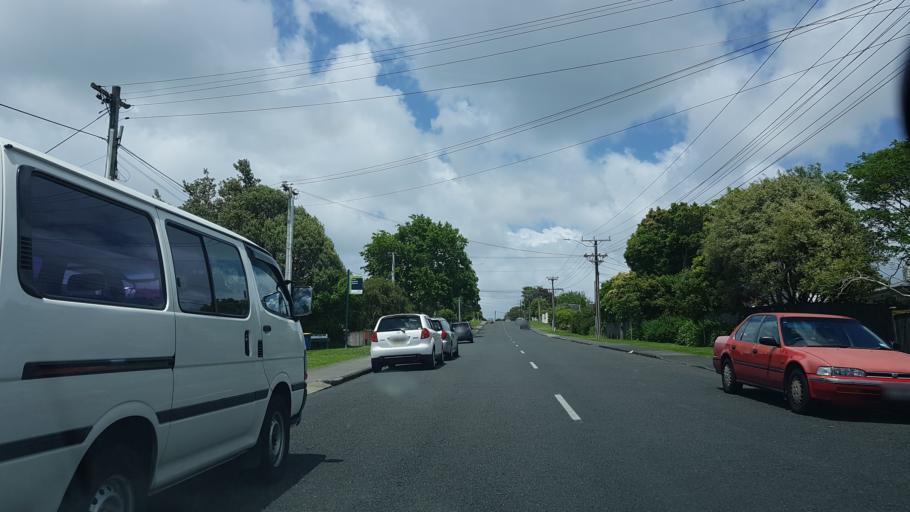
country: NZ
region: Auckland
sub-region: Auckland
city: North Shore
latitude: -36.7972
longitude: 174.7055
